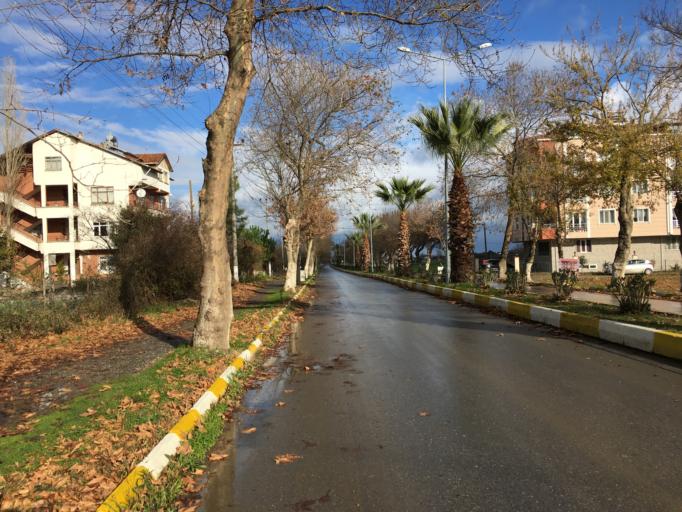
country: TR
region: Samsun
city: Alacam
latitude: 41.6222
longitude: 35.6080
